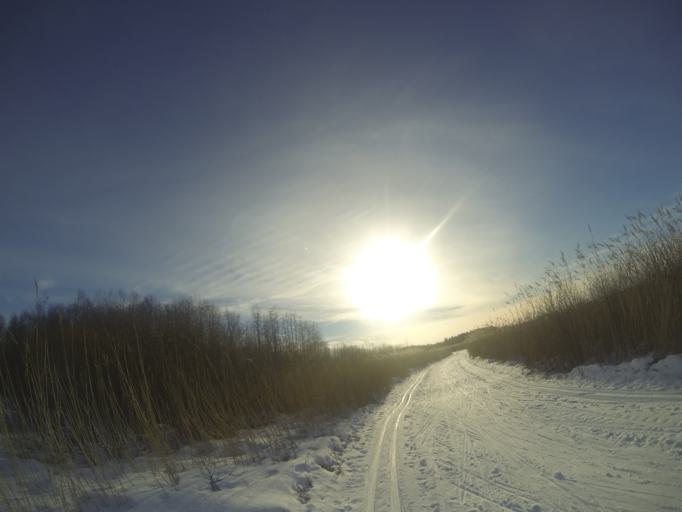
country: FI
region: Southern Savonia
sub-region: Savonlinna
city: Savonlinna
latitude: 61.9110
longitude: 28.9200
